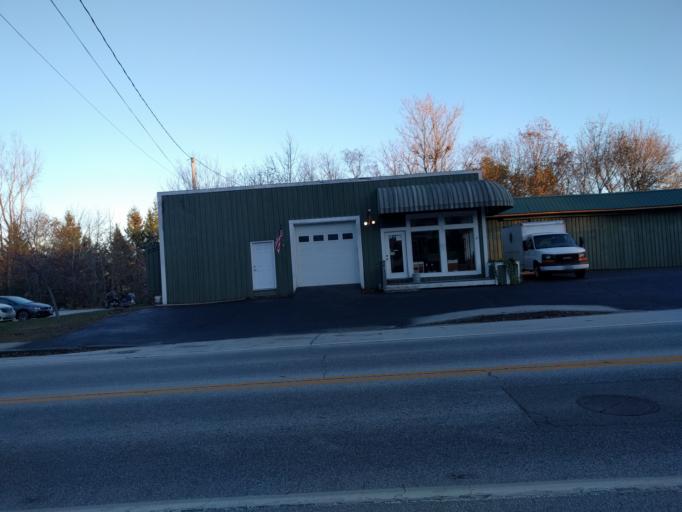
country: US
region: Maine
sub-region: Waldo County
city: Winterport
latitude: 44.6377
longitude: -68.8454
